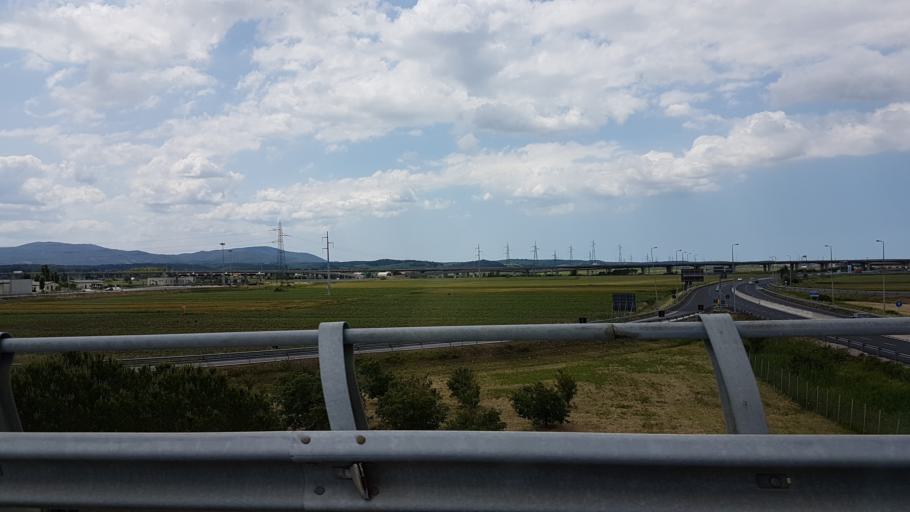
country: IT
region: Tuscany
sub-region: Provincia di Livorno
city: Vicarello
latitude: 43.6190
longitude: 10.4474
